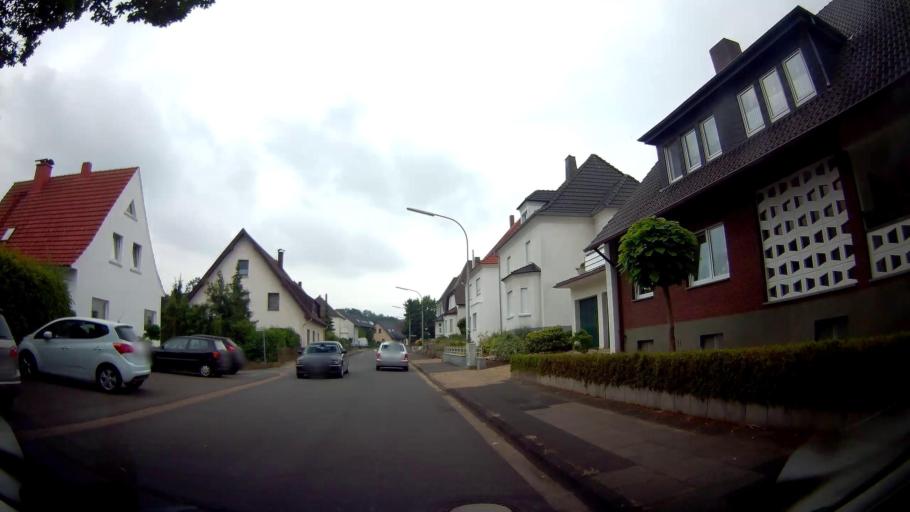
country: DE
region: North Rhine-Westphalia
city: Loehne
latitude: 52.1928
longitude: 8.7188
